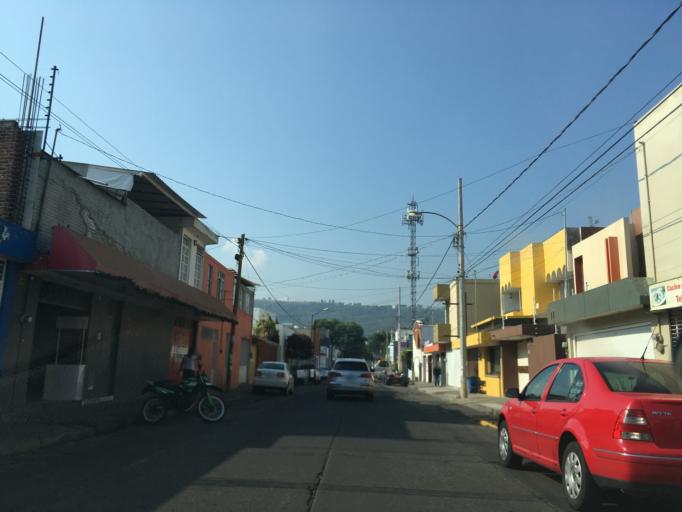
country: MX
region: Michoacan
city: Morelia
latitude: 19.6917
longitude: -101.1697
